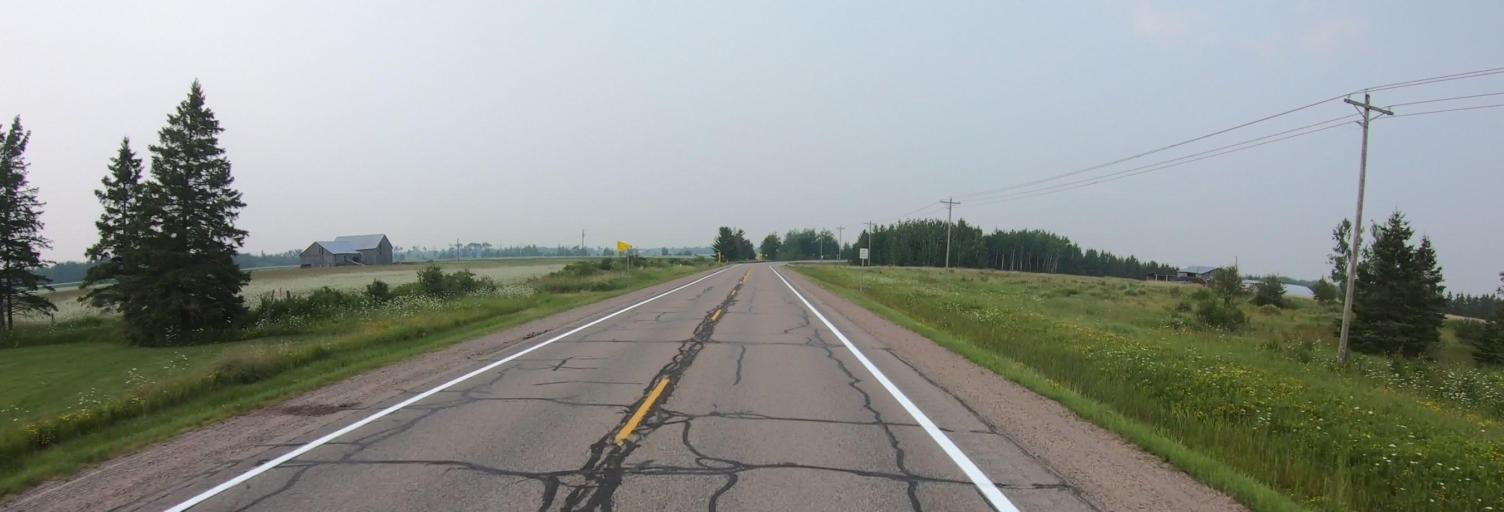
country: US
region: Michigan
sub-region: Chippewa County
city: Sault Ste. Marie
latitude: 46.3645
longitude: -84.3640
